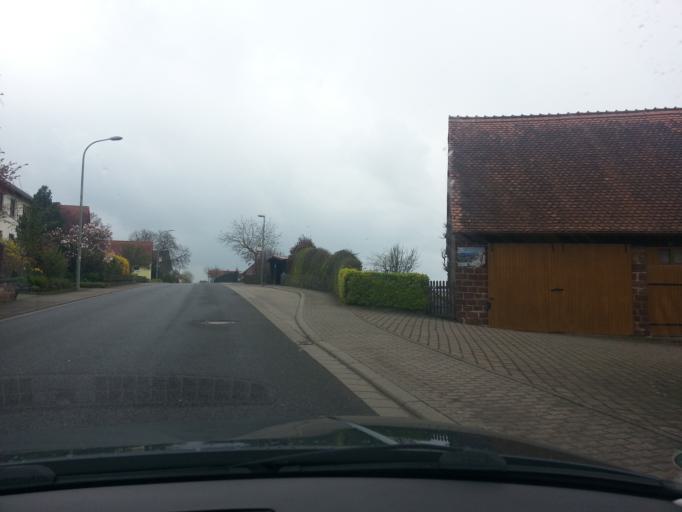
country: DE
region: Rheinland-Pfalz
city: Kashofen
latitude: 49.3287
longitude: 7.4159
